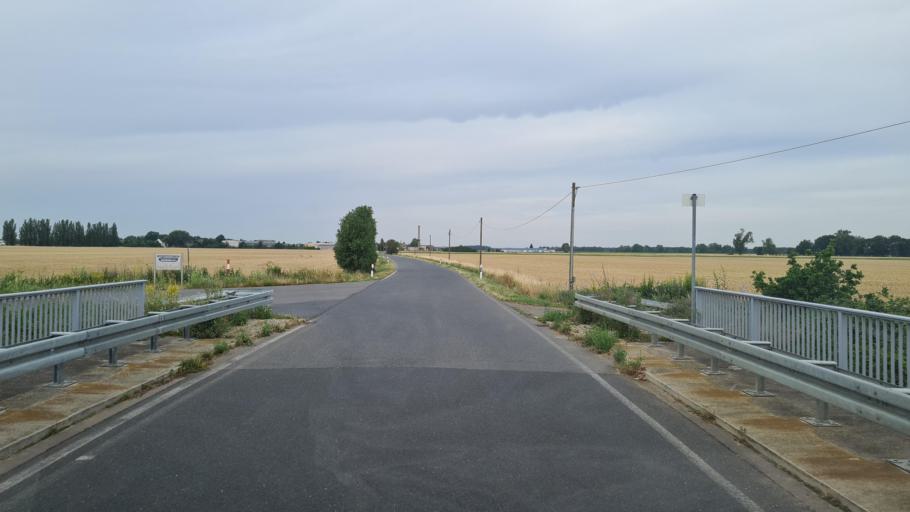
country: DE
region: Saxony-Anhalt
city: Jessen
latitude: 51.7562
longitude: 12.9649
